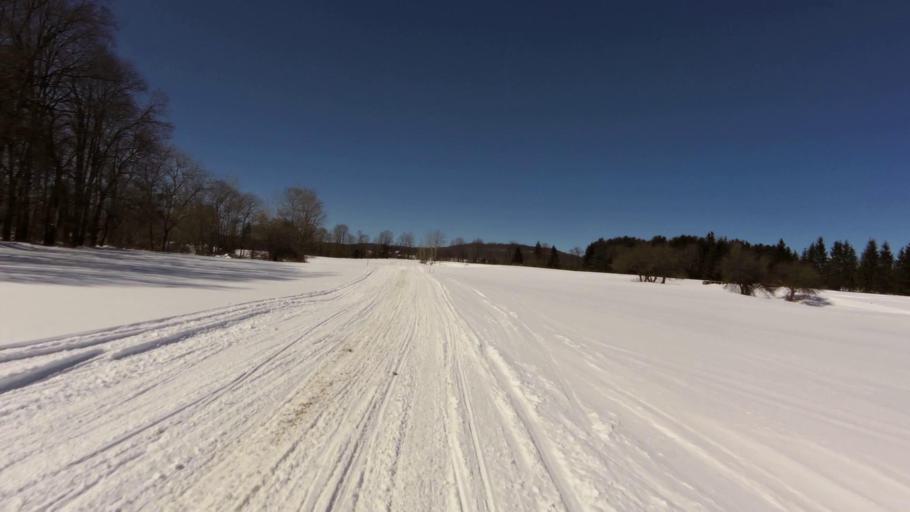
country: US
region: New York
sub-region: Allegany County
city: Houghton
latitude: 42.3869
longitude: -78.2544
